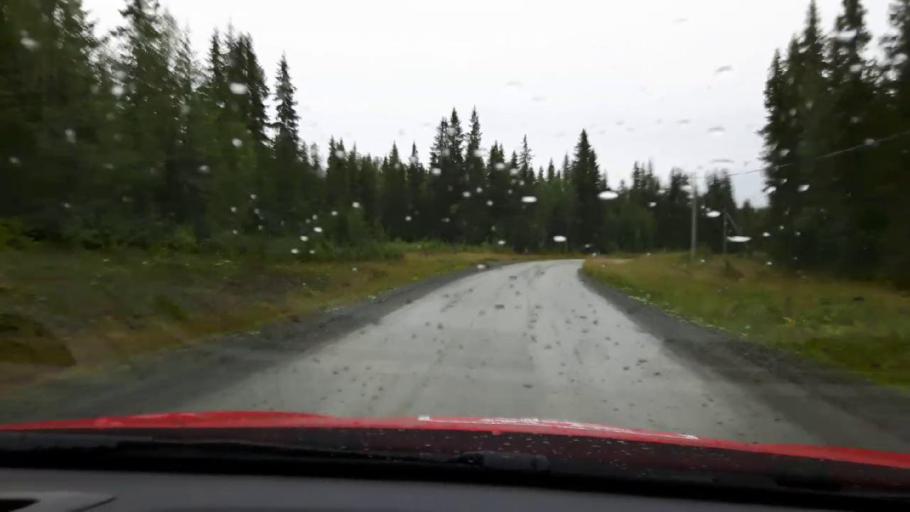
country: SE
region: Jaemtland
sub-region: Are Kommun
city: Are
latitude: 63.4437
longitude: 12.8077
